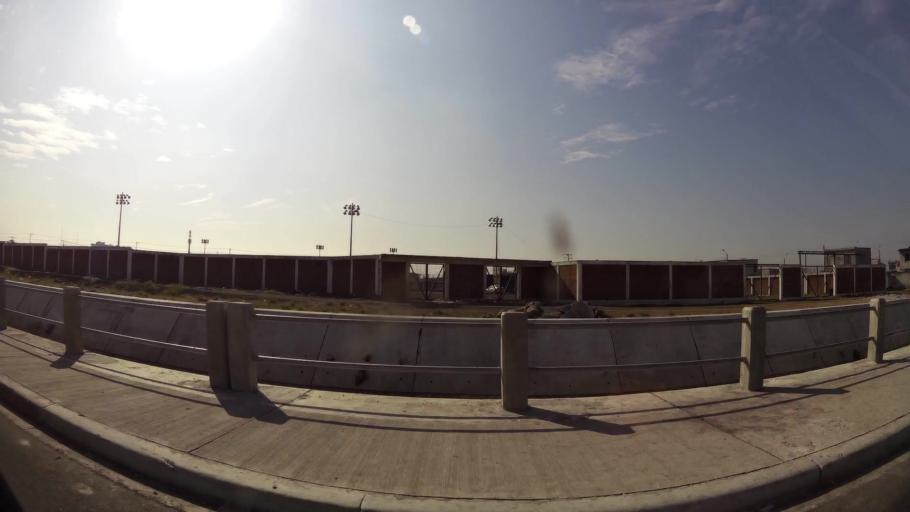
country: EC
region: Guayas
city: Eloy Alfaro
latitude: -2.0820
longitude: -79.9236
